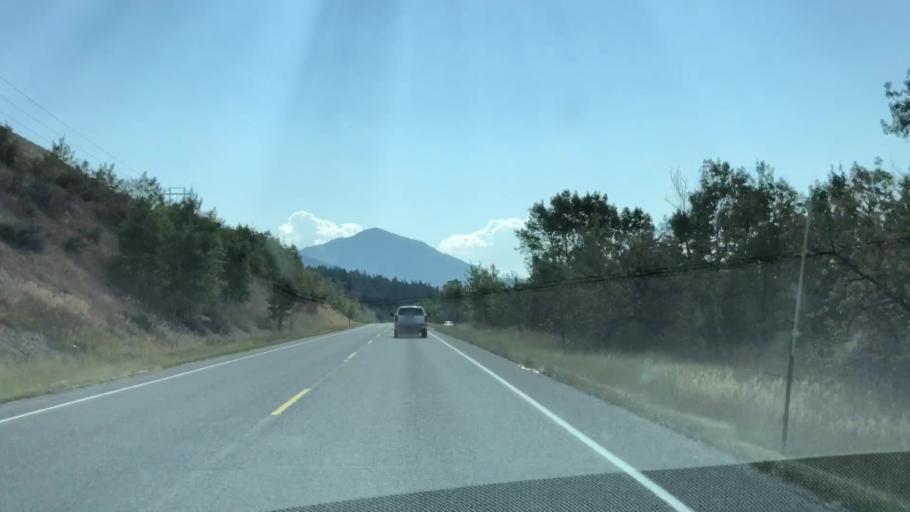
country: US
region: Wyoming
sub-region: Teton County
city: Hoback
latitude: 43.2064
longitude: -111.0528
